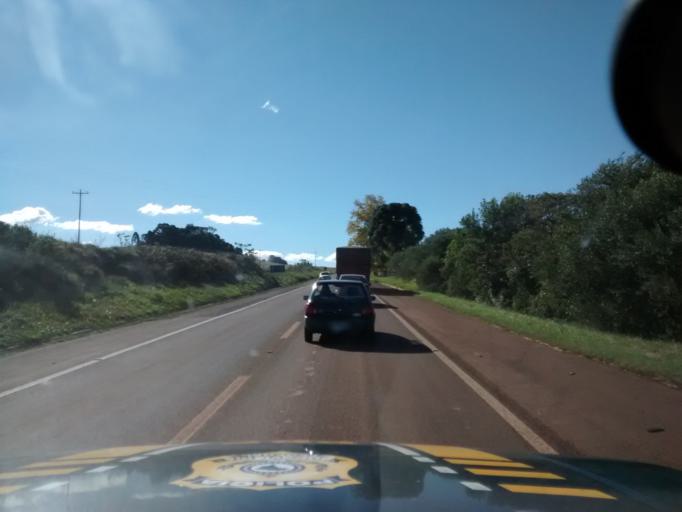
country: BR
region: Rio Grande do Sul
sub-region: Lagoa Vermelha
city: Lagoa Vermelha
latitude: -28.2944
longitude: -51.4628
